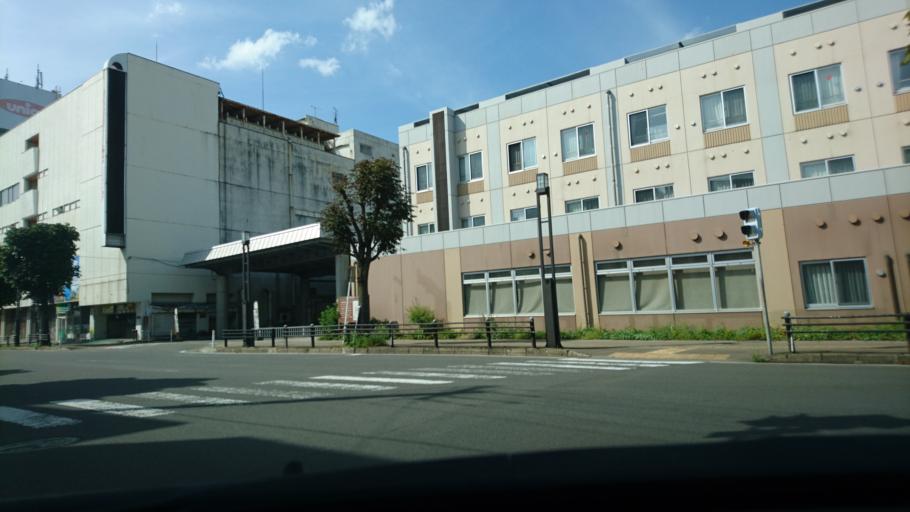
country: JP
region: Akita
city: Yokotemachi
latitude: 39.3104
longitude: 140.5628
